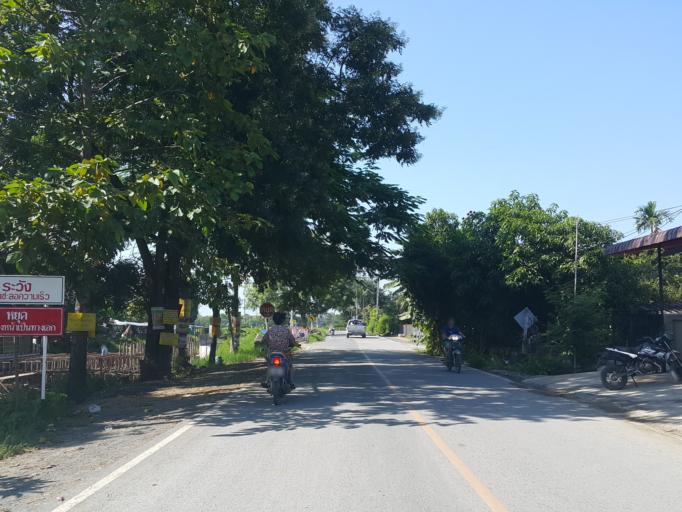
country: TH
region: Chiang Mai
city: Mae On
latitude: 18.8217
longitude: 99.1728
